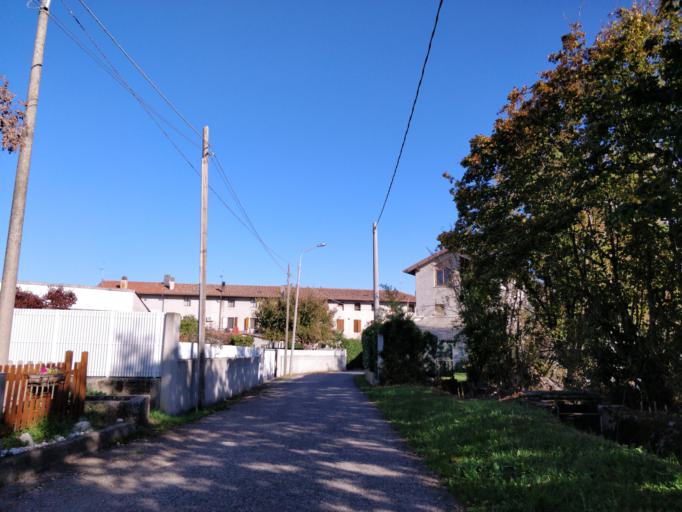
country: IT
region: Friuli Venezia Giulia
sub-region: Provincia di Udine
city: Bertiolo
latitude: 45.9451
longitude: 13.0458
